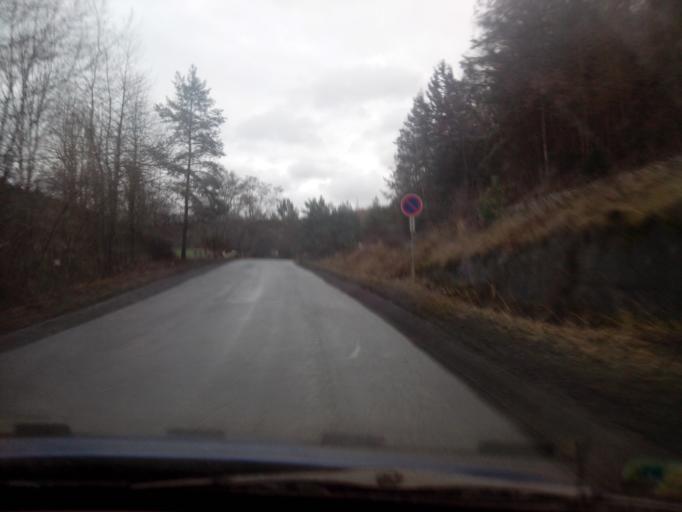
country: CZ
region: Central Bohemia
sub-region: Okres Beroun
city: Kraluv Dvur
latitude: 49.9355
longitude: 14.0428
